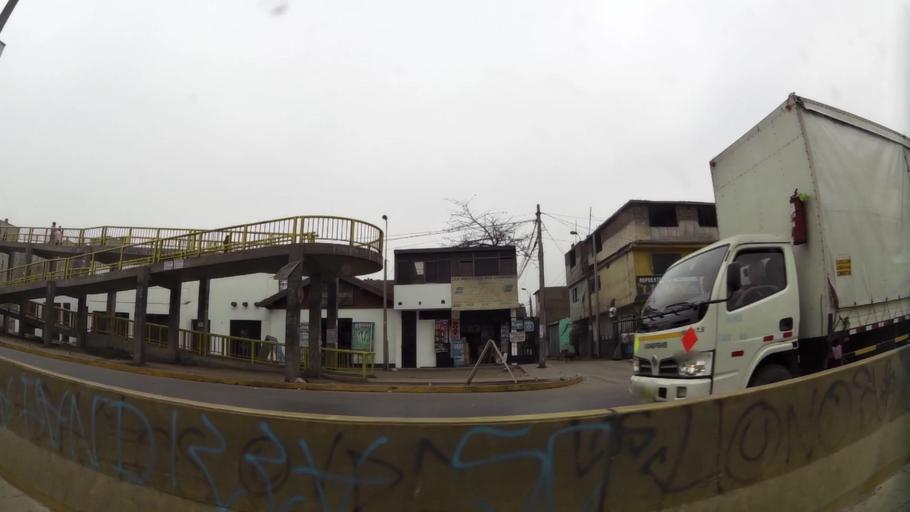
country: PE
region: Lima
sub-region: Lima
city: Santa Maria
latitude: -12.0195
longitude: -76.8995
